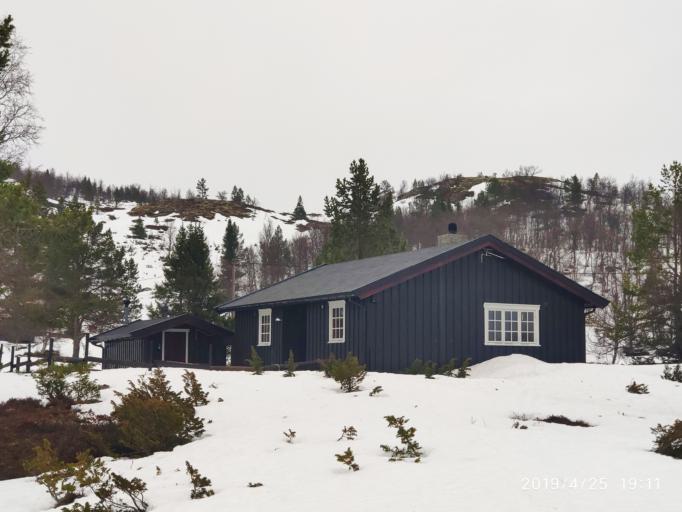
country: NO
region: Oppland
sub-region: Sel
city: Otta
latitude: 61.7903
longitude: 9.6129
